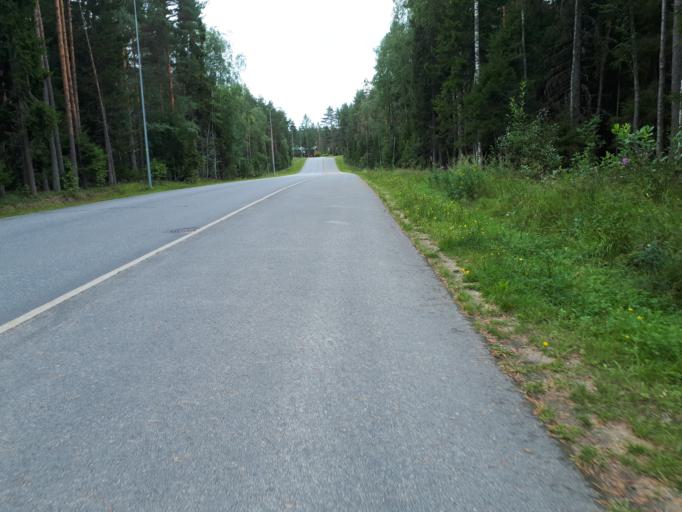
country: FI
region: Northern Ostrobothnia
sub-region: Oulunkaari
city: Ii
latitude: 65.3213
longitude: 25.4099
